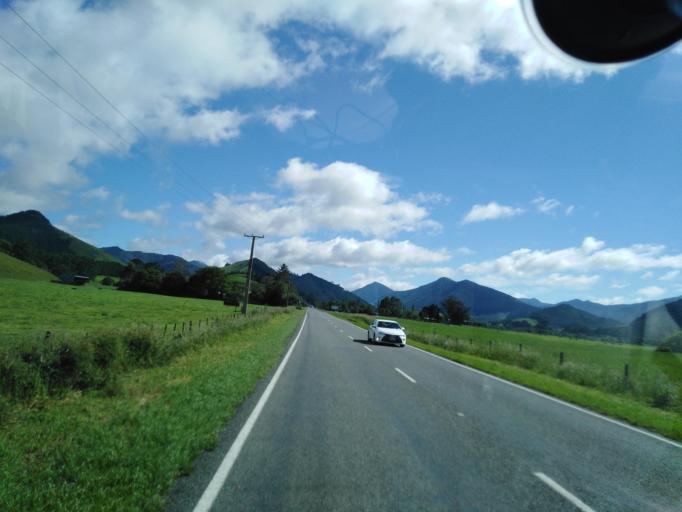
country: NZ
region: Nelson
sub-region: Nelson City
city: Nelson
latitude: -41.2425
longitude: 173.5782
